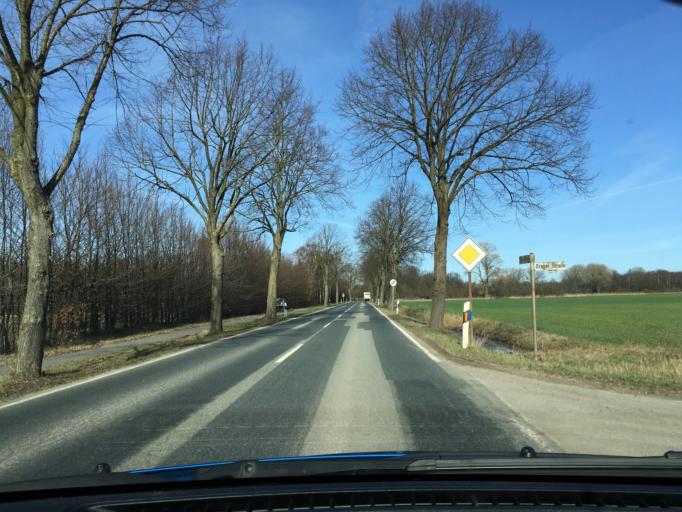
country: DE
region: Lower Saxony
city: Drage
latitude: 53.3886
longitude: 10.2463
